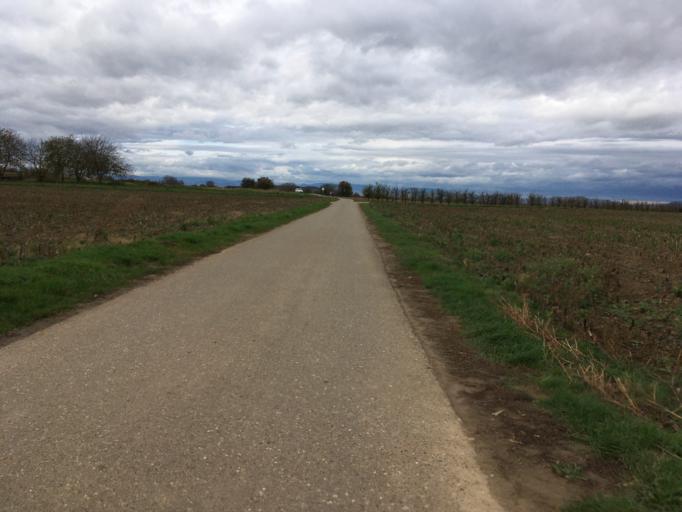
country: DE
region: Baden-Wuerttemberg
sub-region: Freiburg Region
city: Endingen
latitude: 48.1473
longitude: 7.6827
